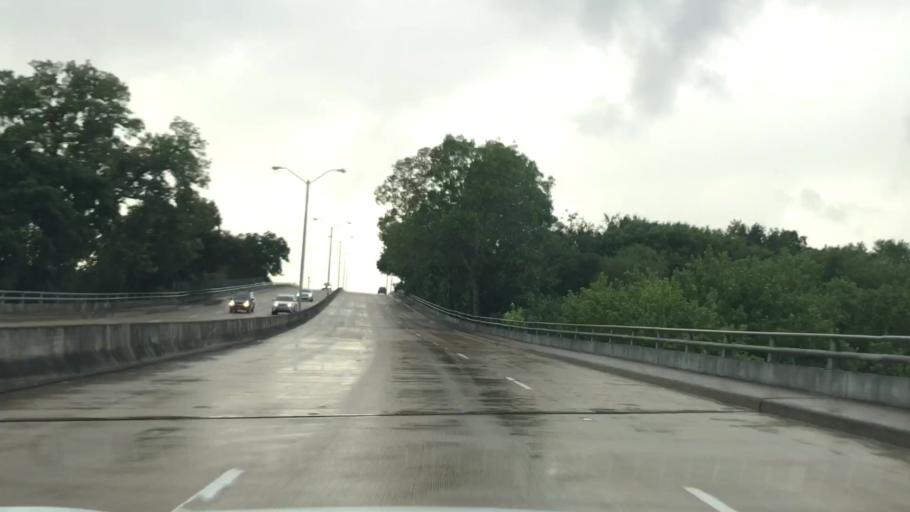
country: US
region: Texas
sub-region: Dallas County
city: Richardson
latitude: 32.8987
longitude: -96.7632
